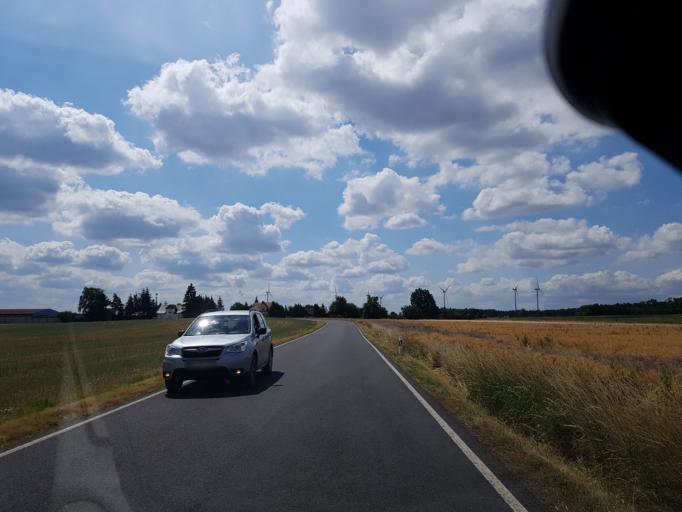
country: DE
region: Brandenburg
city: Drebkau
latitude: 51.6728
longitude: 14.2806
